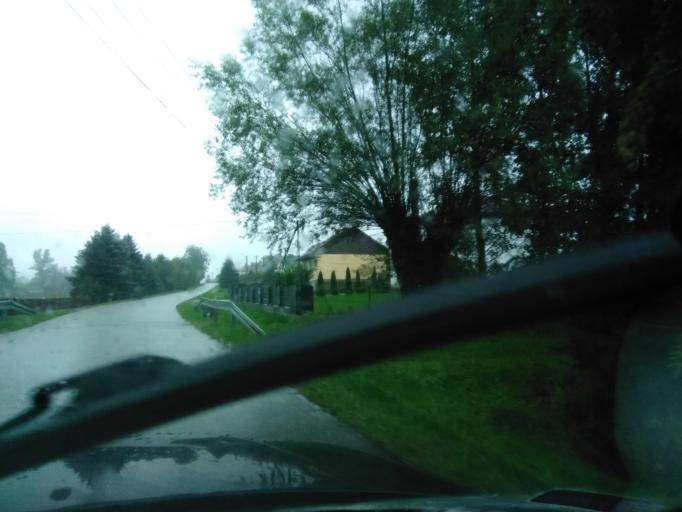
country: PL
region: Subcarpathian Voivodeship
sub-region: Powiat ropczycko-sedziszowski
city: Niedzwiada
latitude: 50.0016
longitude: 21.5507
